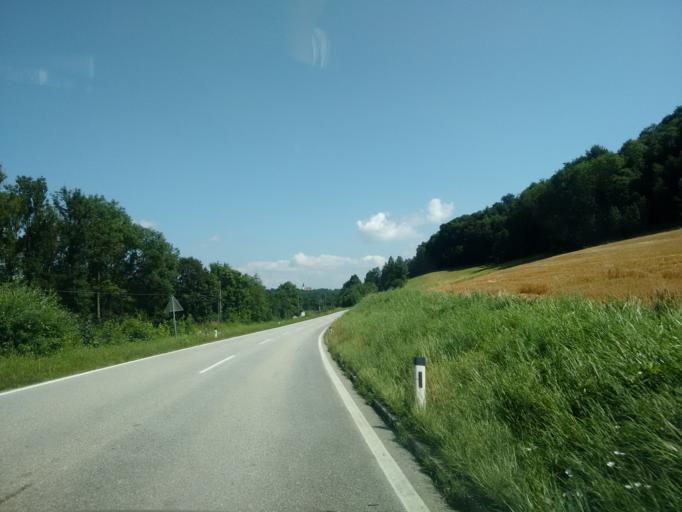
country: AT
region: Upper Austria
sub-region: Politischer Bezirk Kirchdorf an der Krems
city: Kremsmunster
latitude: 48.0428
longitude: 14.1271
